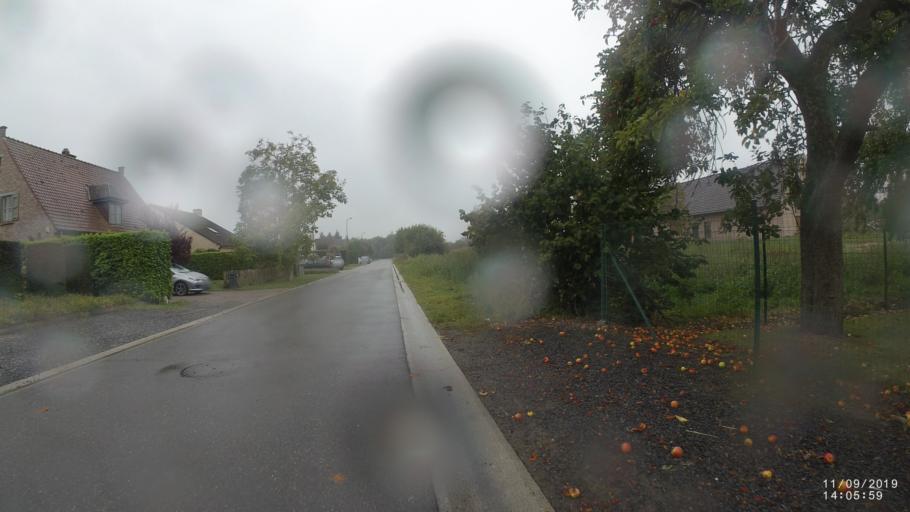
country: BE
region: Flanders
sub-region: Provincie Oost-Vlaanderen
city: Evergem
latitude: 51.0867
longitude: 3.6829
